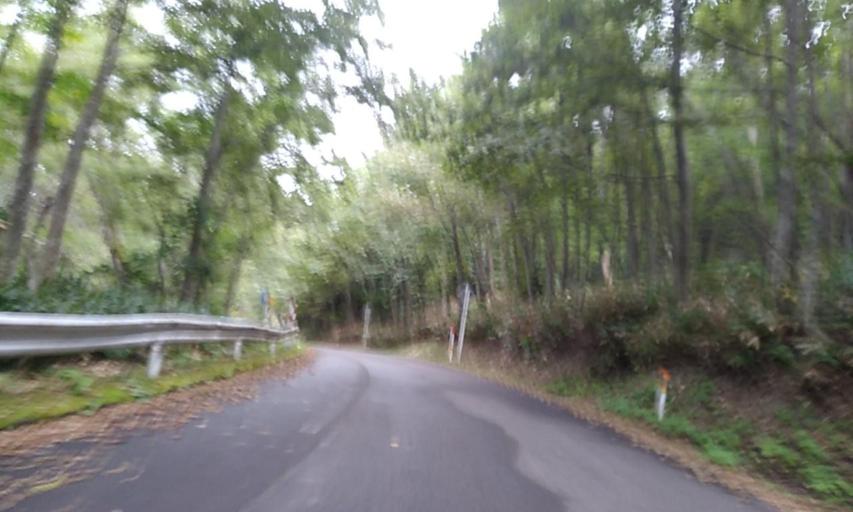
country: JP
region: Hokkaido
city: Bihoro
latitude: 43.5719
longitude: 144.2022
